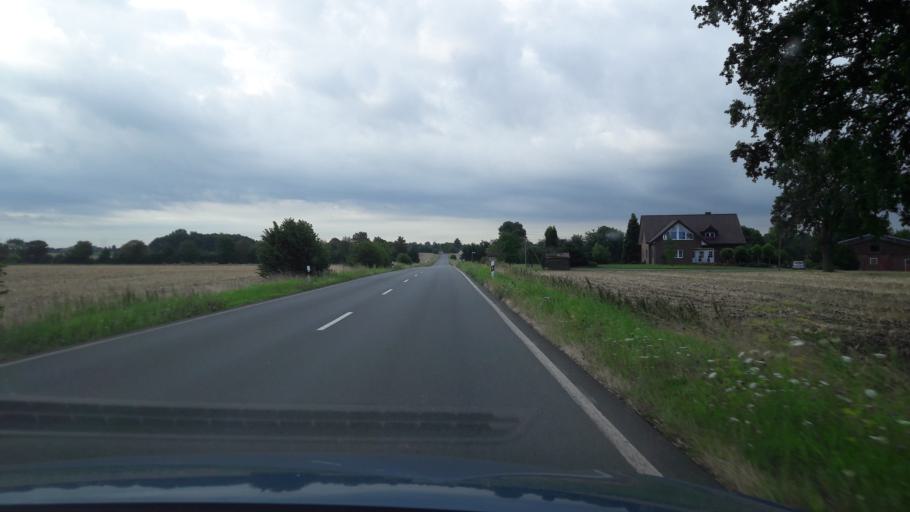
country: DE
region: North Rhine-Westphalia
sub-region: Regierungsbezirk Munster
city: Ennigerloh
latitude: 51.8466
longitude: 7.9987
